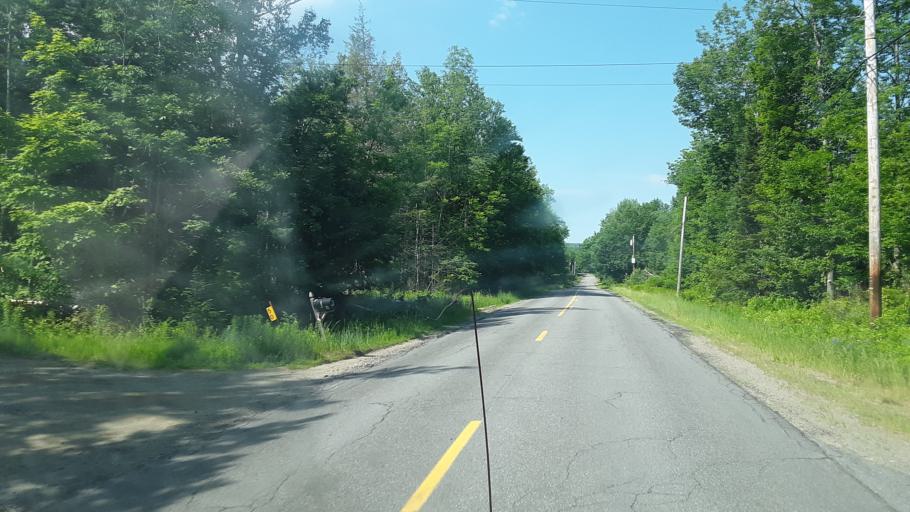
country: US
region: Maine
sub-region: Waldo County
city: Swanville
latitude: 44.5503
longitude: -68.9641
